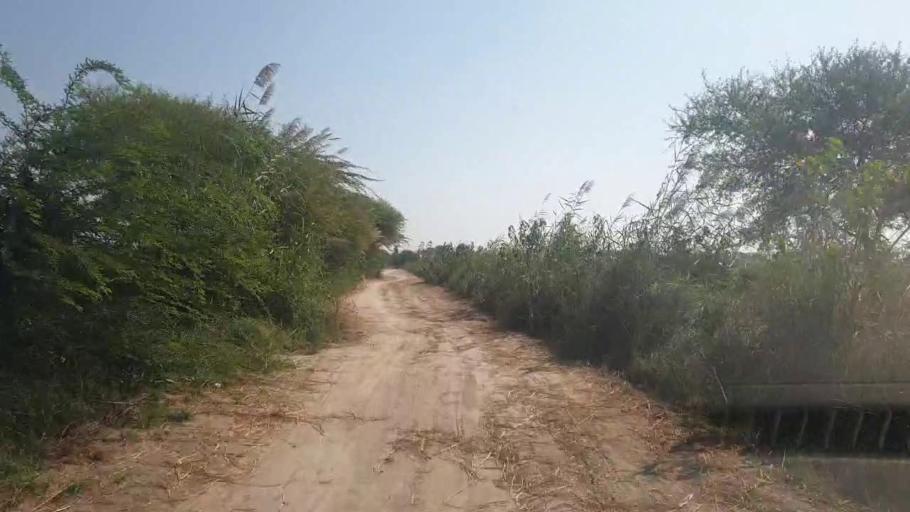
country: PK
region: Sindh
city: Badin
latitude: 24.7123
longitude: 68.8773
